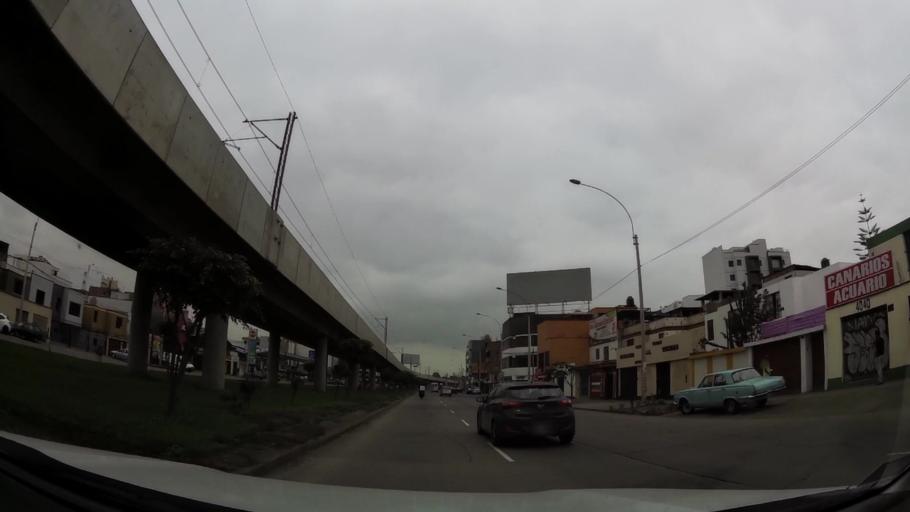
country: PE
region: Lima
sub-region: Lima
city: Surco
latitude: -12.1171
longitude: -76.9989
